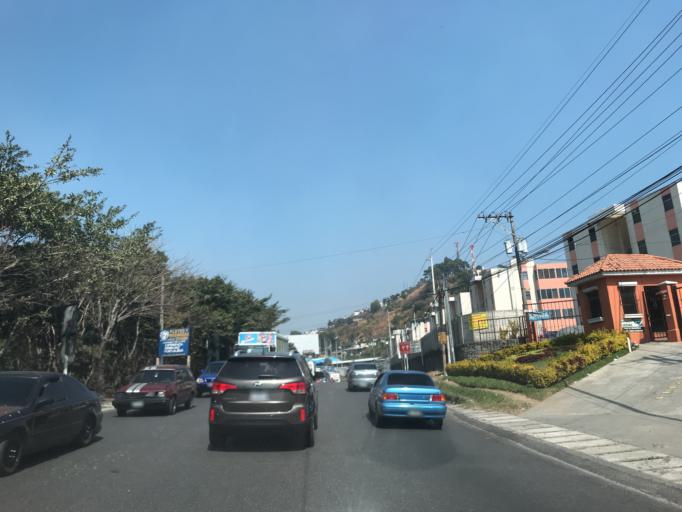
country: GT
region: Guatemala
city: Villa Nueva
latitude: 14.5362
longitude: -90.5566
